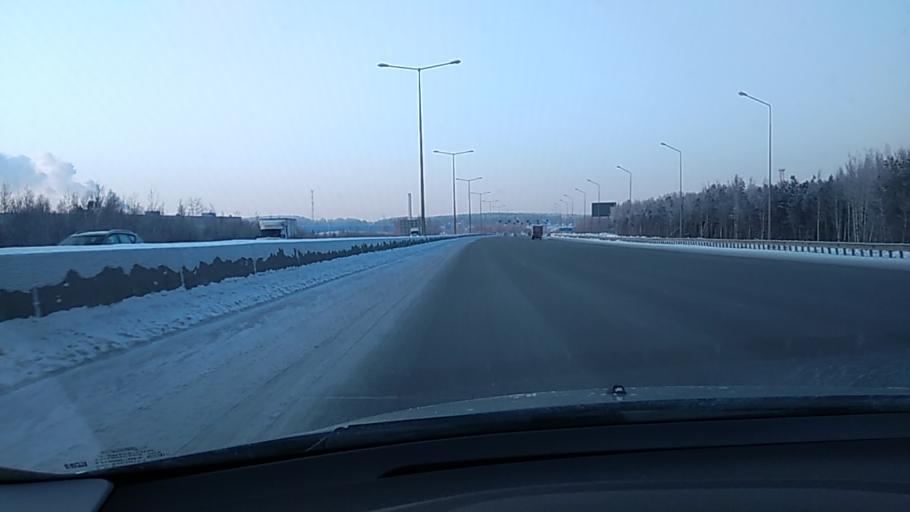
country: RU
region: Sverdlovsk
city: Istok
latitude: 56.7626
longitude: 60.7579
